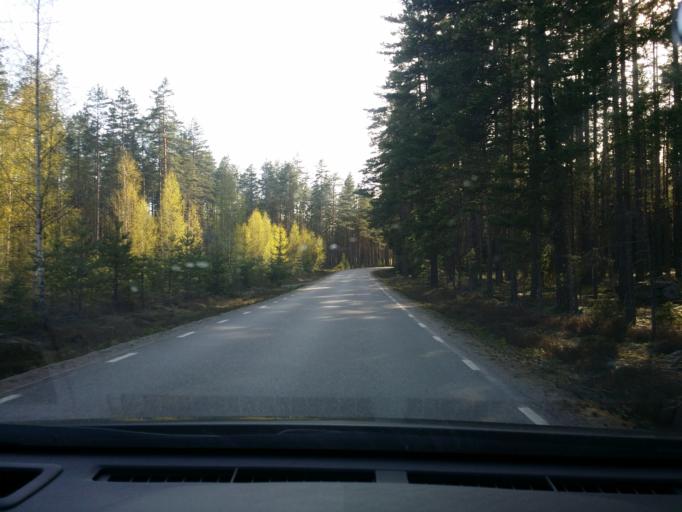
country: SE
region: Dalarna
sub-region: Avesta Kommun
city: Avesta
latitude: 60.0644
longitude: 16.3399
